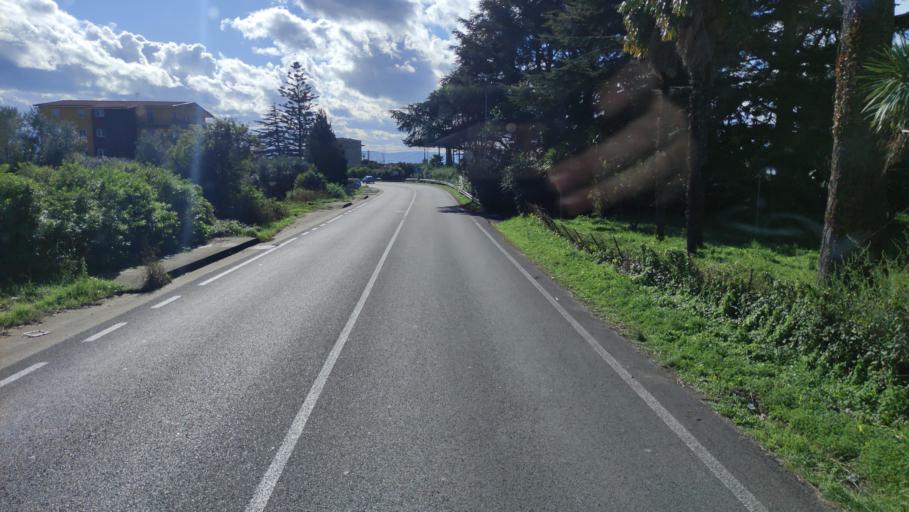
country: IT
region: Calabria
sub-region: Provincia di Catanzaro
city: Santa Eufemia Lamezia
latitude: 38.9313
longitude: 16.2862
